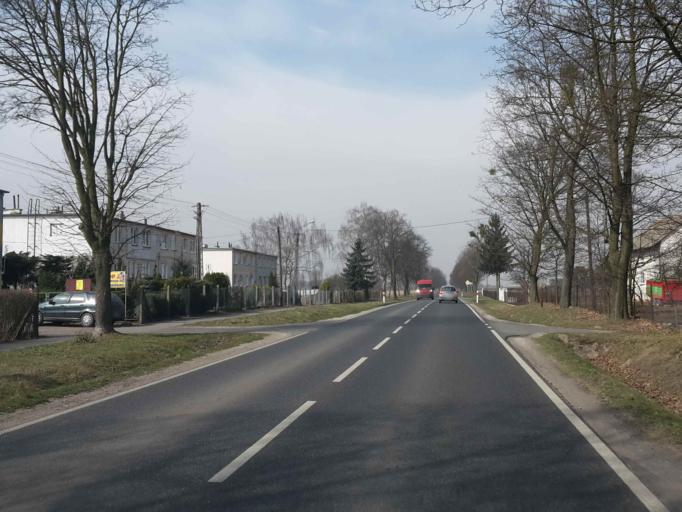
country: PL
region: Kujawsko-Pomorskie
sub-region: Powiat nakielski
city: Szubin
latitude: 53.0780
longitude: 17.6904
